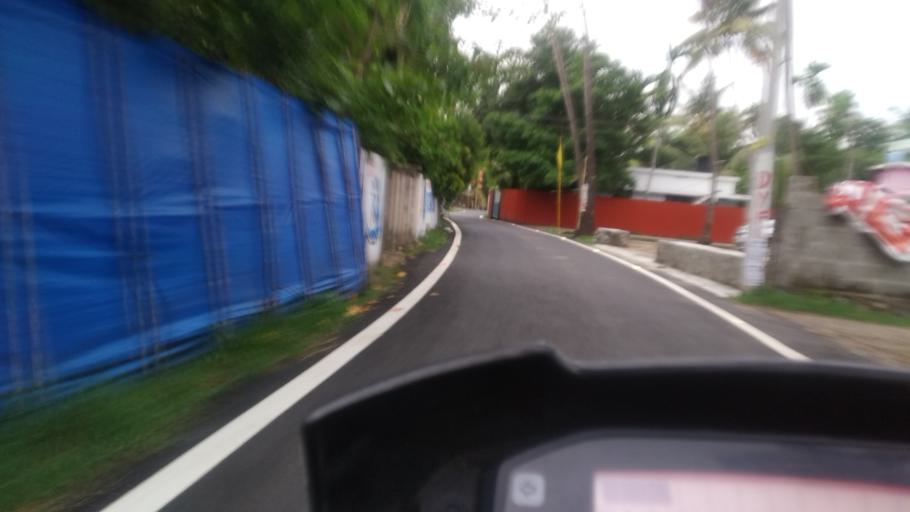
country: IN
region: Kerala
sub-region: Ernakulam
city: Elur
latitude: 10.0755
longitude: 76.2215
